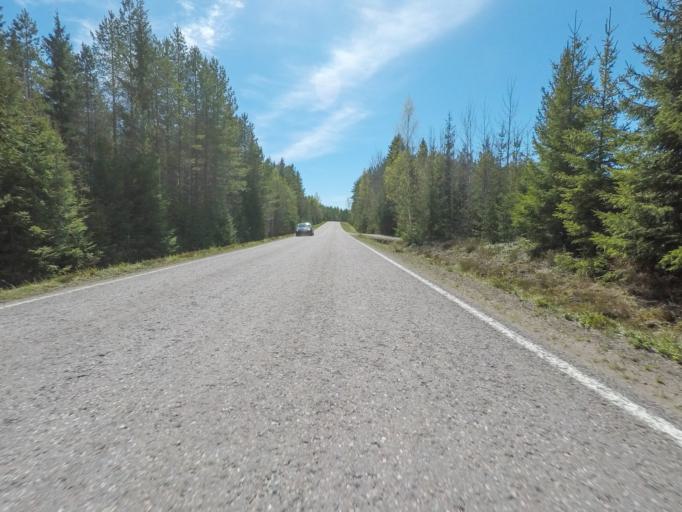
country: FI
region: Uusimaa
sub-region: Helsinki
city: Kaerkoelae
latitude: 60.5950
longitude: 23.8008
